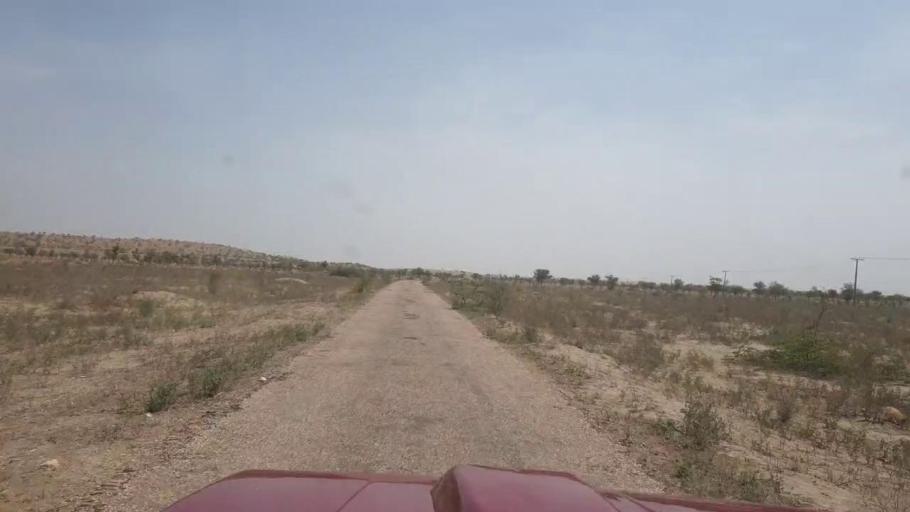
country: PK
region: Sindh
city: Islamkot
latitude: 25.1297
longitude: 70.3839
